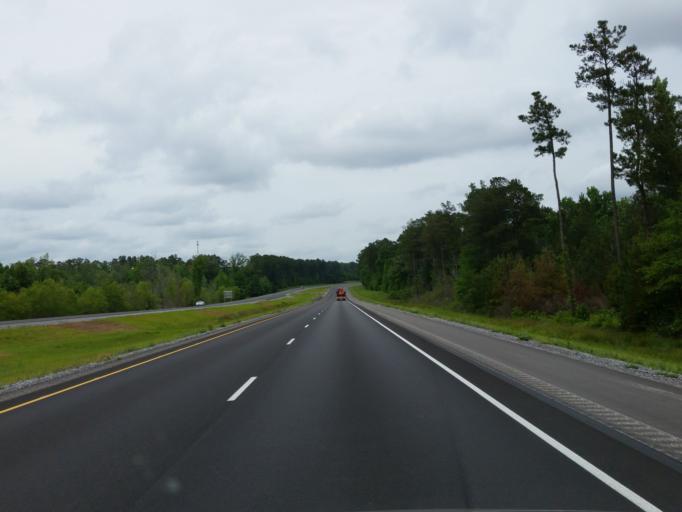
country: US
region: Mississippi
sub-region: Jones County
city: Sharon
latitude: 31.8666
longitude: -89.0461
